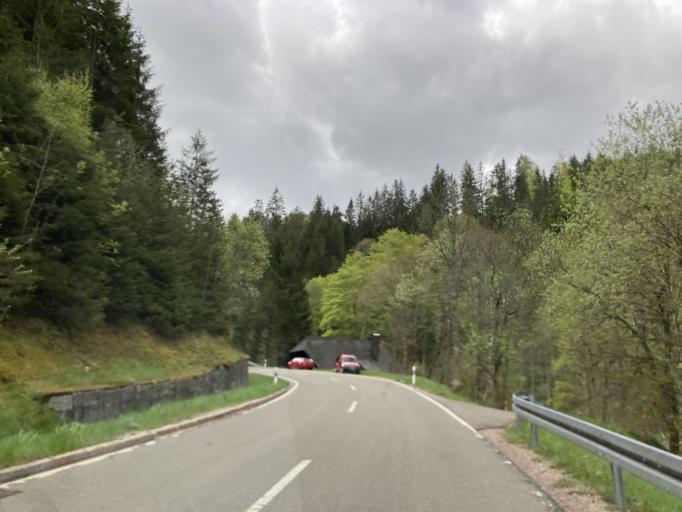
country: DE
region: Baden-Wuerttemberg
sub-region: Freiburg Region
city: Schonach im Schwarzwald
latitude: 48.1490
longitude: 8.1581
